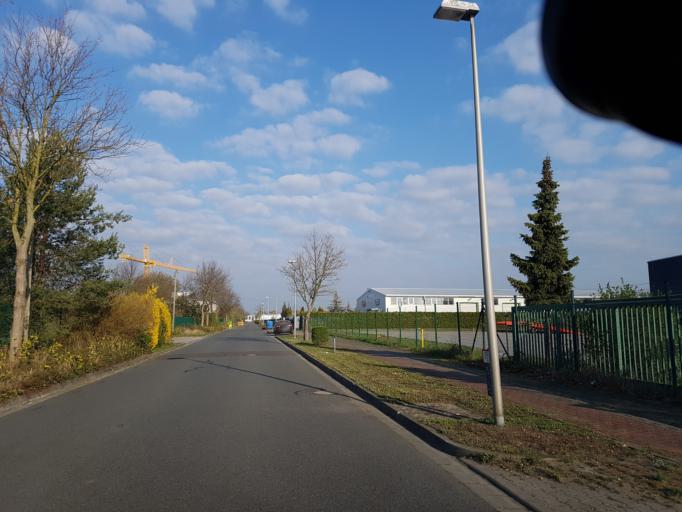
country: DE
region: Brandenburg
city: Linthe
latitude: 52.1659
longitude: 12.7835
